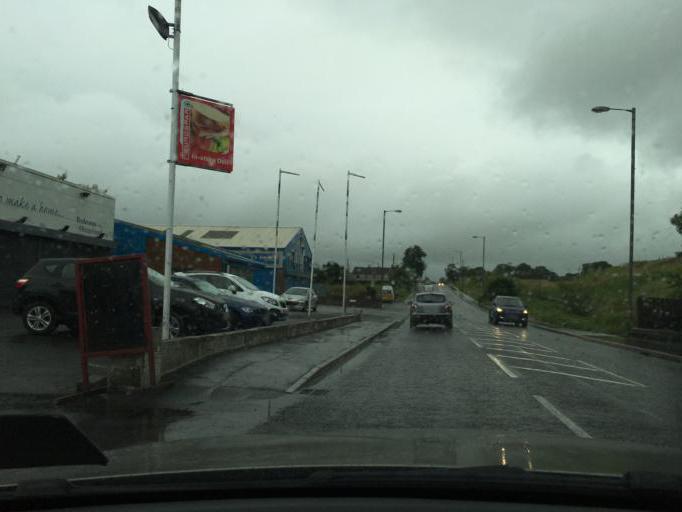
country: GB
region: Northern Ireland
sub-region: Fermanagh District
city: Enniskillen
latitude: 54.3571
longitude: -7.6362
